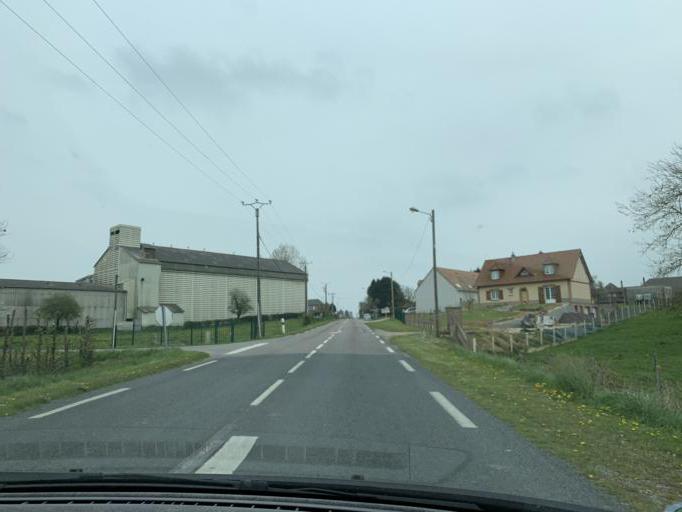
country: FR
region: Haute-Normandie
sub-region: Departement de la Seine-Maritime
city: Londinieres
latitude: 49.8434
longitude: 1.4720
